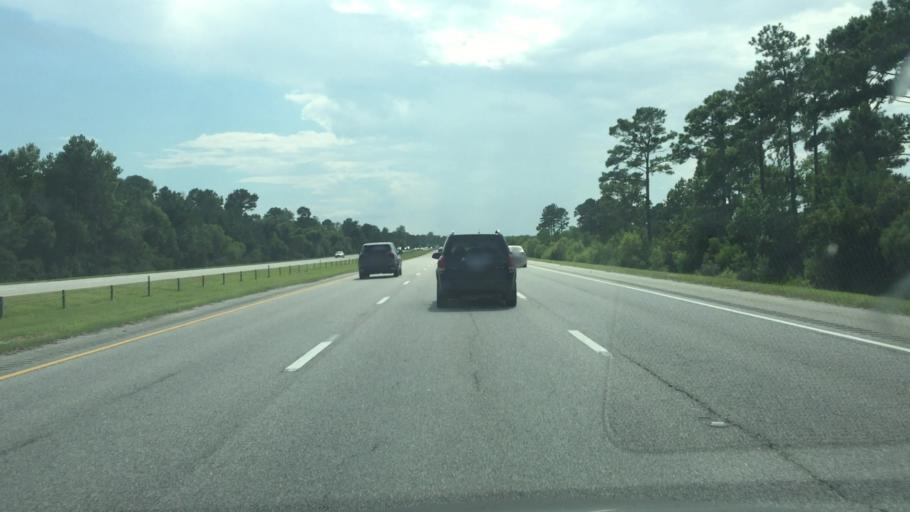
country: US
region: South Carolina
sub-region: Horry County
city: Myrtle Beach
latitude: 33.7768
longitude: -78.8143
